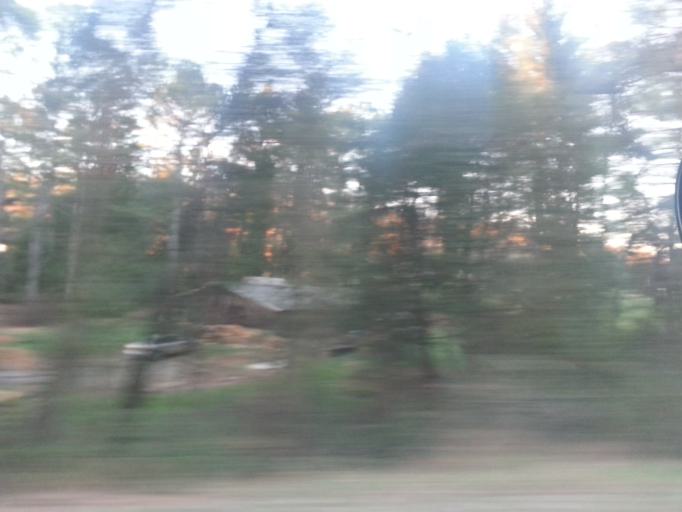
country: US
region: Tennessee
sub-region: Blount County
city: Eagleton Village
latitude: 35.8323
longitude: -83.9315
